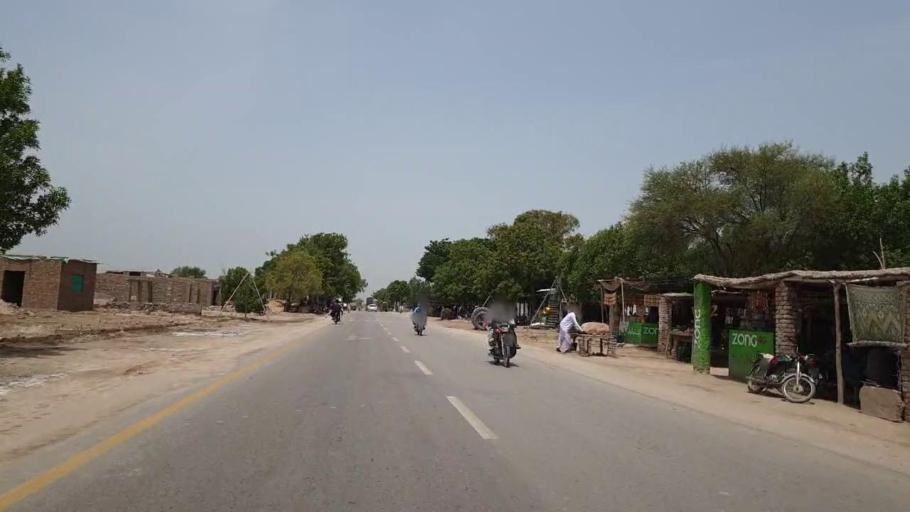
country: PK
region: Sindh
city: Nawabshah
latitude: 26.2461
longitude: 68.4577
